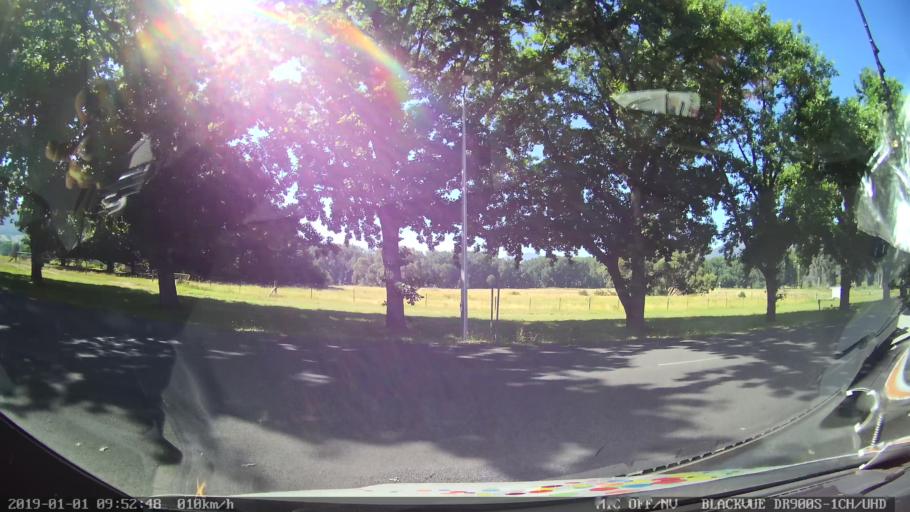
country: AU
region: New South Wales
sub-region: Snowy River
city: Jindabyne
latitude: -36.2195
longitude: 148.1247
